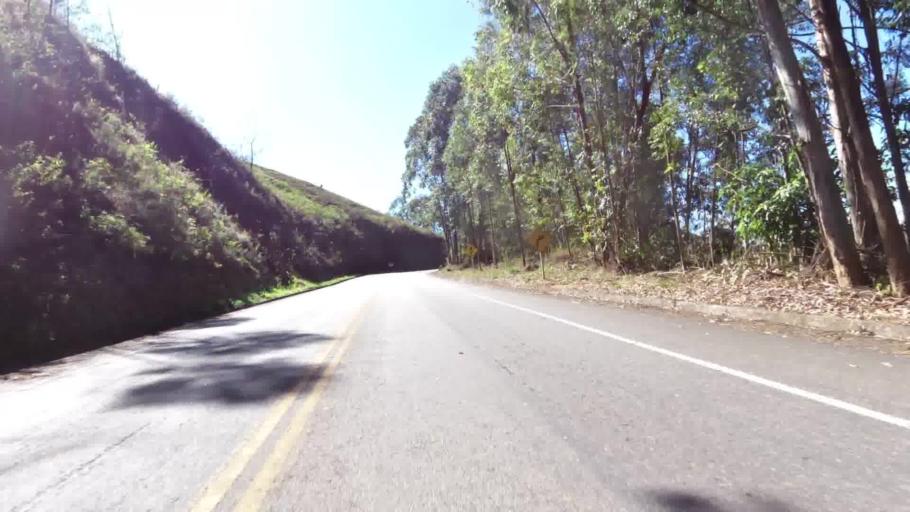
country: BR
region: Espirito Santo
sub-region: Vargem Alta
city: Vargem Alta
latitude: -20.6942
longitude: -40.9335
